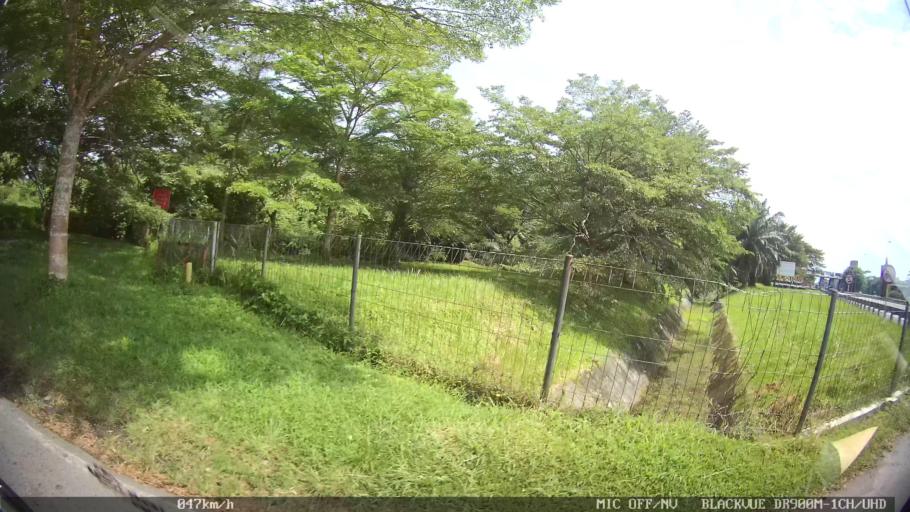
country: ID
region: North Sumatra
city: Percut
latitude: 3.6127
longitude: 98.8557
